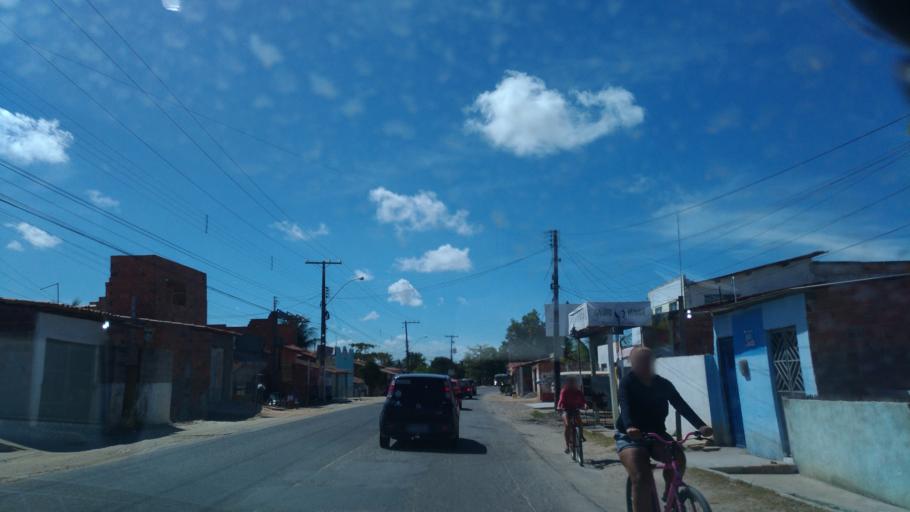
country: BR
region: Alagoas
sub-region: Marechal Deodoro
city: Marechal Deodoro
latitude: -9.7607
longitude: -35.8660
